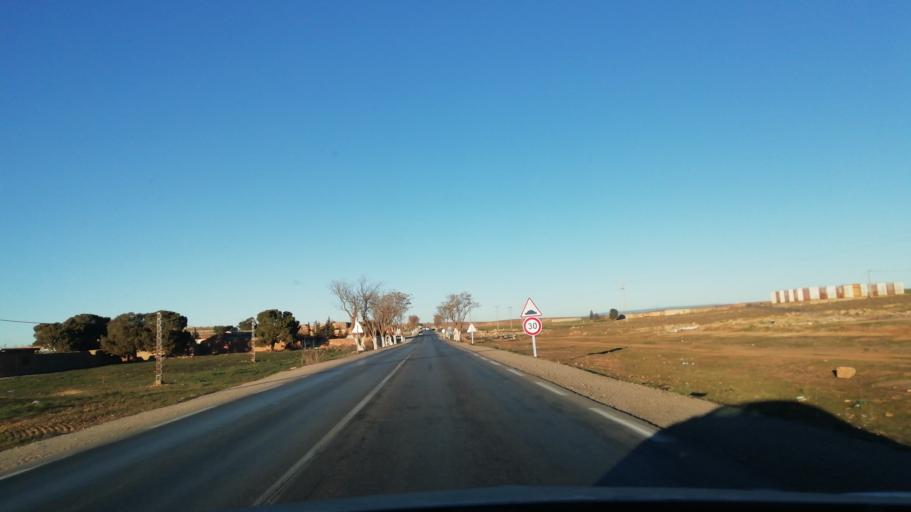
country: DZ
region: Saida
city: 'Ain el Hadjar
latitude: 34.5763
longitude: 0.1282
